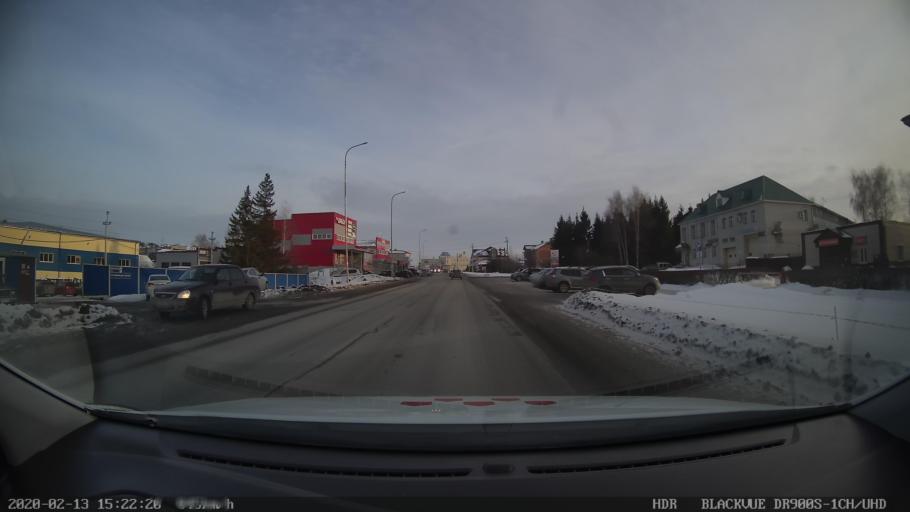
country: RU
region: Tatarstan
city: Vysokaya Gora
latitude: 55.9214
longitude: 49.3076
